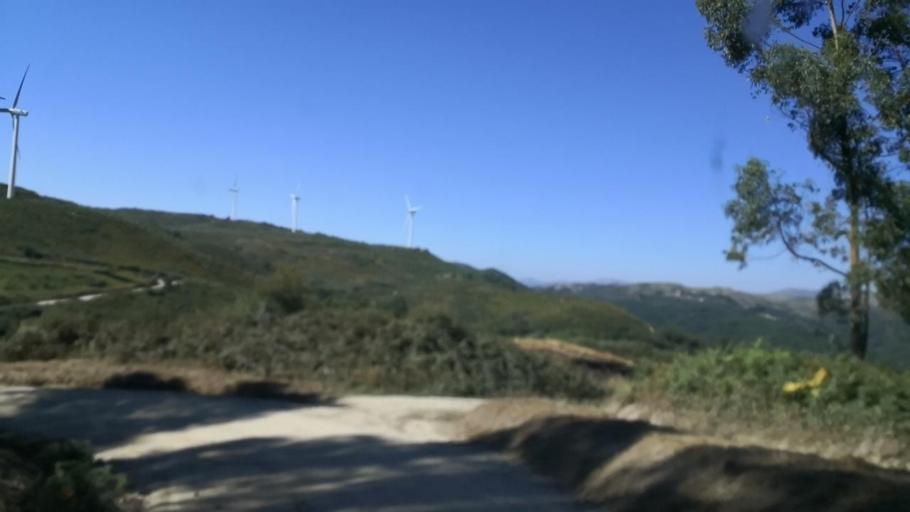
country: PT
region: Braga
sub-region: Cabeceiras de Basto
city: Refojos de Basto
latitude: 41.4970
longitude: -8.0741
